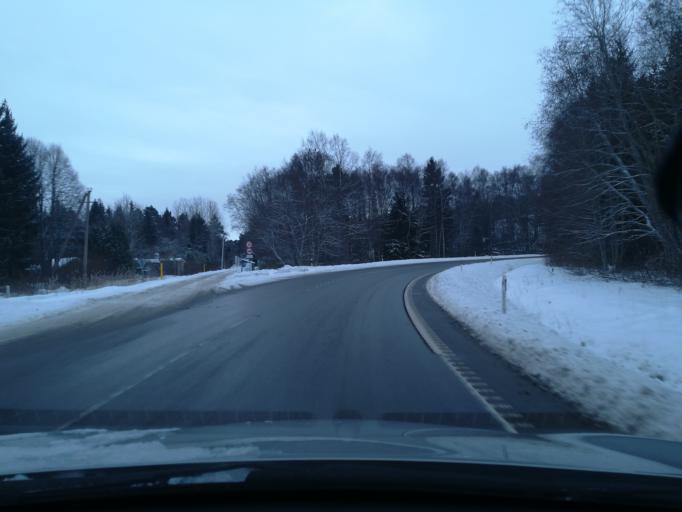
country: EE
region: Harju
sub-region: Keila linn
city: Keila
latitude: 59.4159
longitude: 24.3441
